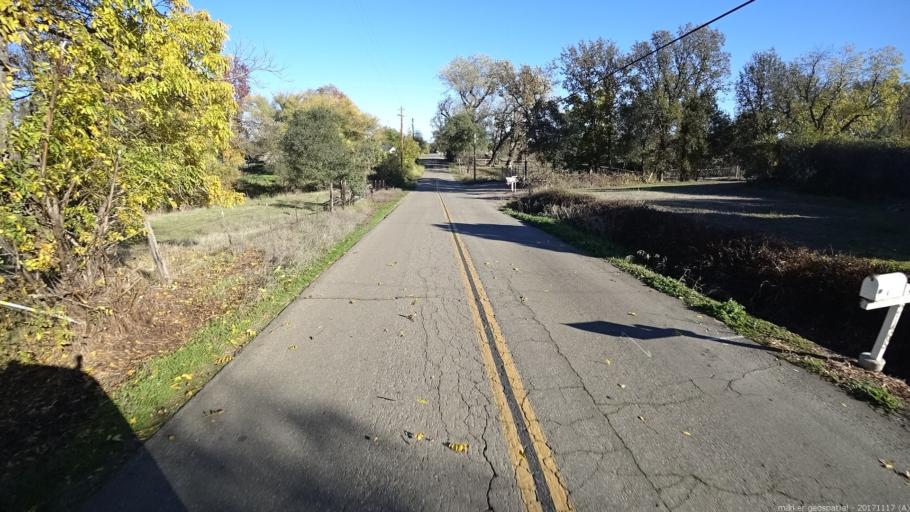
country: US
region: California
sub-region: Shasta County
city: Cottonwood
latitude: 40.3893
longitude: -122.2565
